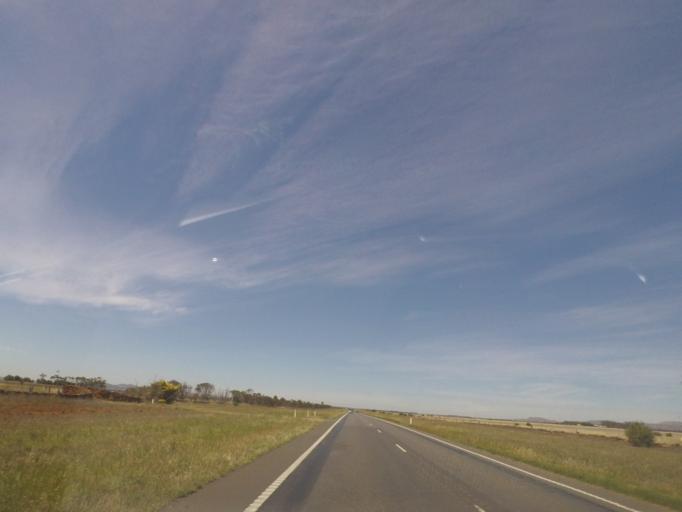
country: AU
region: Victoria
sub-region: Wyndham
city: Wyndham Vale
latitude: -37.8185
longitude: 144.3979
